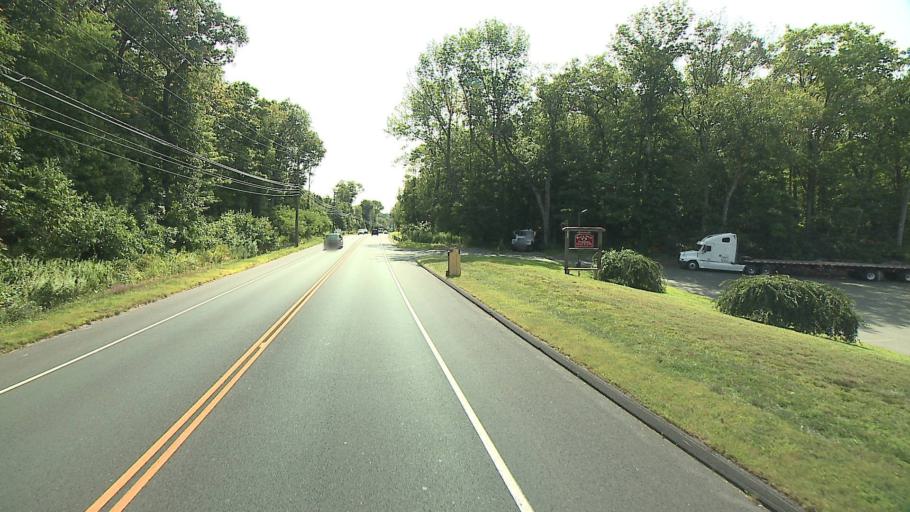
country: US
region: Connecticut
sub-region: Fairfield County
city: Newtown
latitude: 41.3801
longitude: -73.2817
